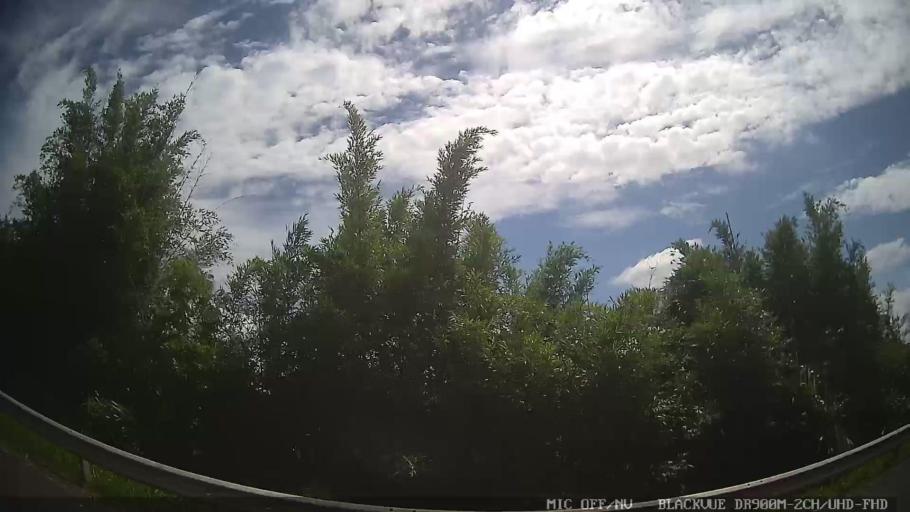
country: BR
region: Sao Paulo
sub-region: Laranjal Paulista
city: Laranjal Paulista
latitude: -23.0409
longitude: -47.8293
